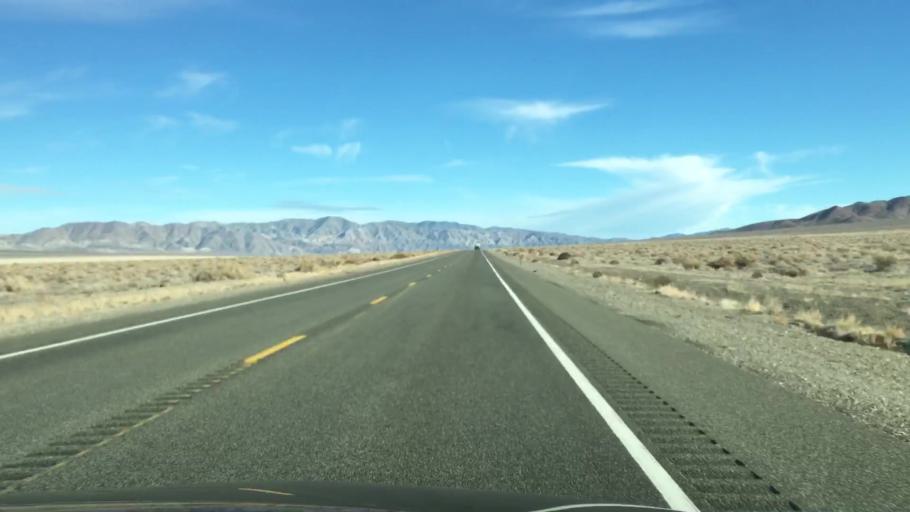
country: US
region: Nevada
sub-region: Mineral County
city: Hawthorne
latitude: 38.5370
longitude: -118.3345
